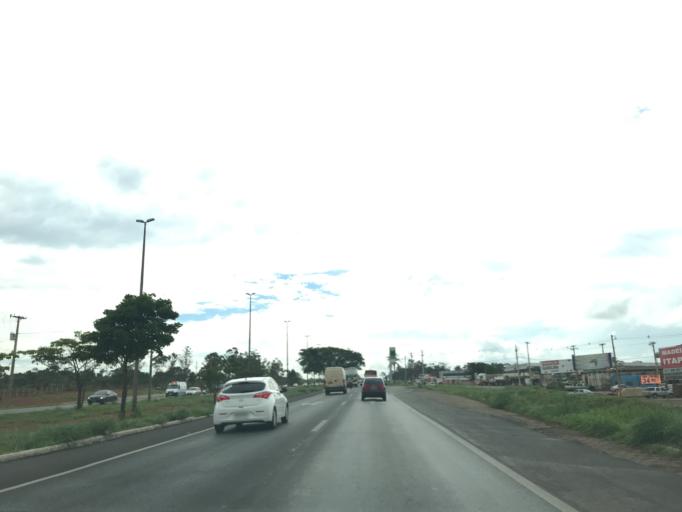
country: BR
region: Federal District
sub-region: Brasilia
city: Brasilia
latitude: -15.6816
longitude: -47.8376
